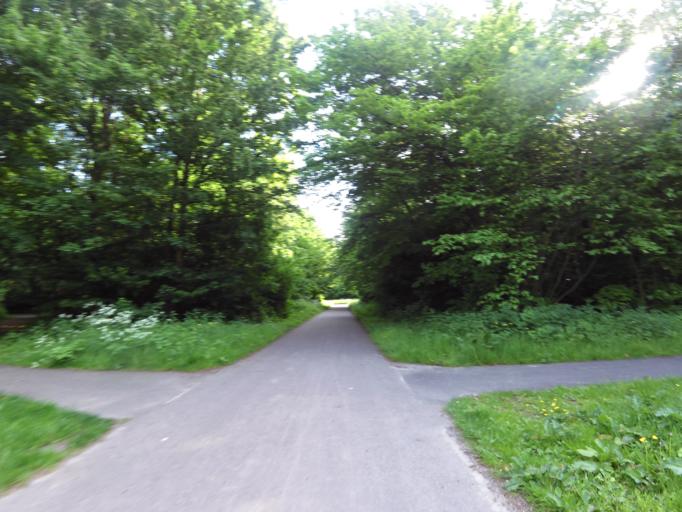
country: NL
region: South Holland
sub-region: Gemeente Pijnacker-Nootdorp
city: Pijnacker
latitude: 52.0551
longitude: 4.4470
